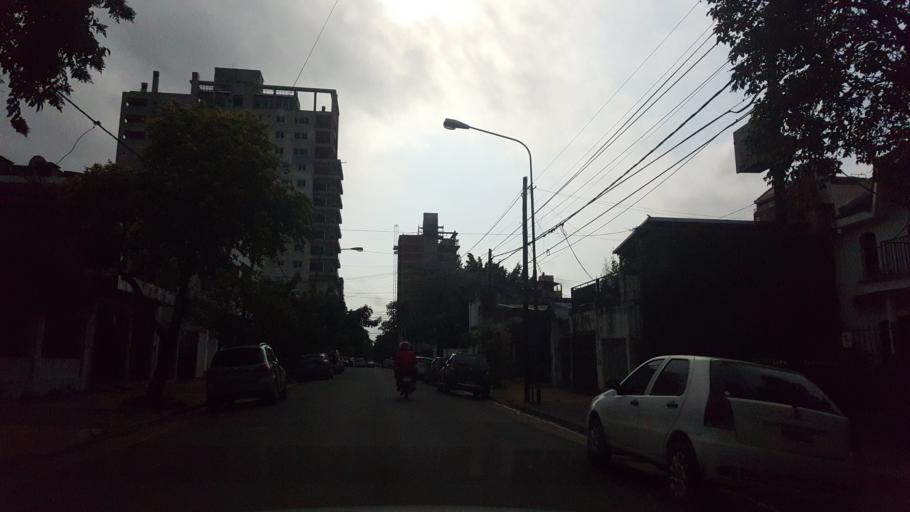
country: AR
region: Misiones
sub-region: Departamento de Capital
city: Posadas
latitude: -27.3713
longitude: -55.8893
